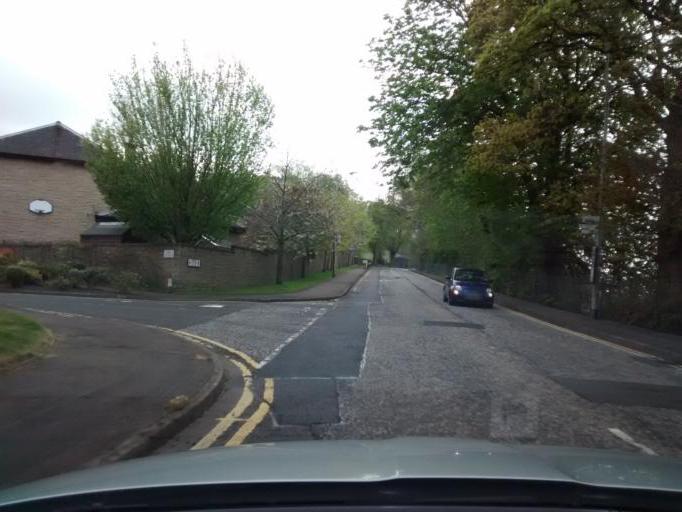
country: GB
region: Scotland
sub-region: Edinburgh
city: Colinton
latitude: 55.9182
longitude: -3.2268
